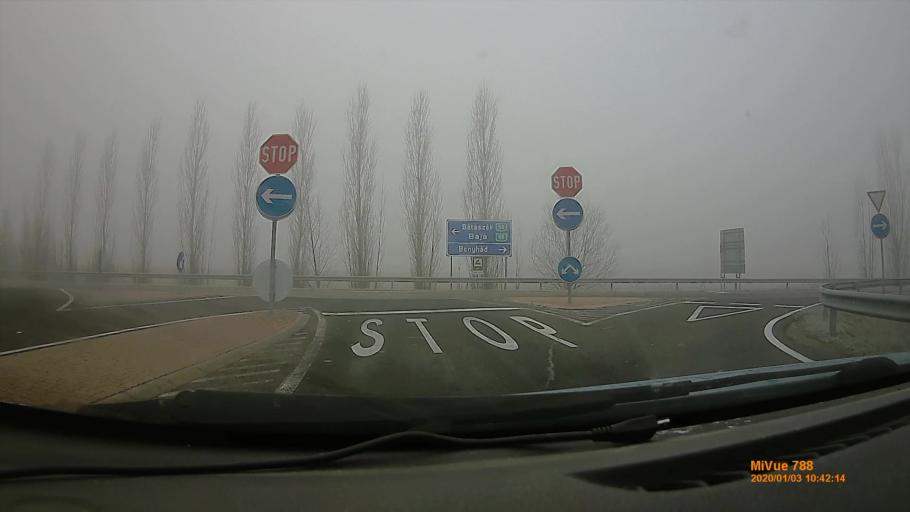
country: HU
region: Tolna
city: Bataszek
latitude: 46.2095
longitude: 18.6993
